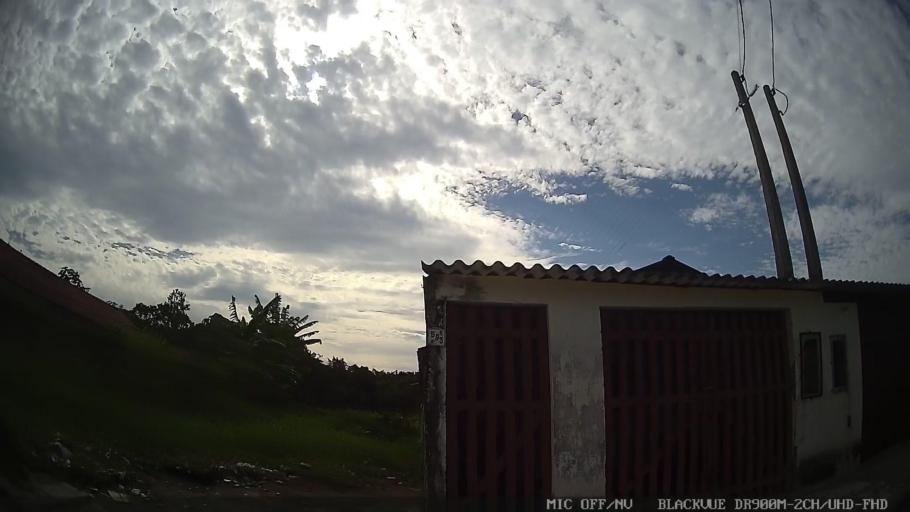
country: BR
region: Sao Paulo
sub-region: Itanhaem
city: Itanhaem
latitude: -24.1596
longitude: -46.7589
